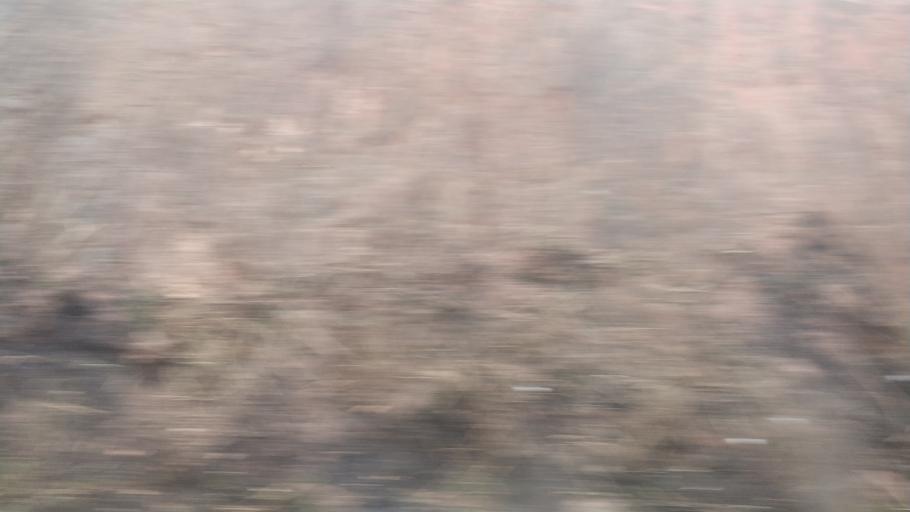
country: BR
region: Rio de Janeiro
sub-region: Seropedica
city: Seropedica
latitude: -22.7522
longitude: -43.6948
